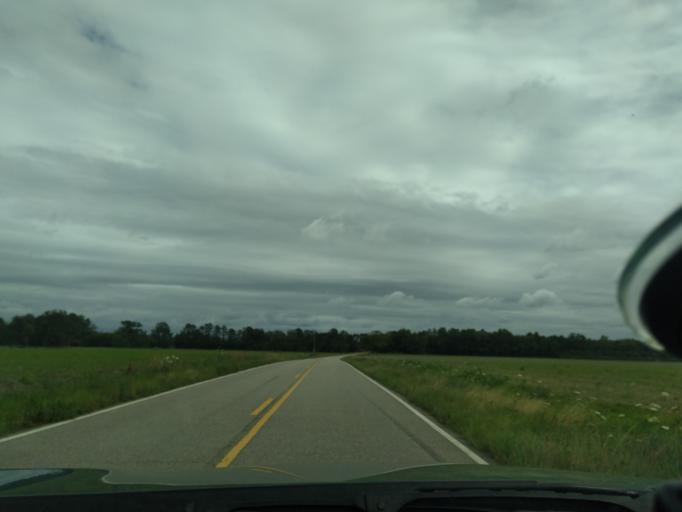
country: US
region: North Carolina
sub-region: Washington County
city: Plymouth
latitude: 35.8780
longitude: -76.7077
